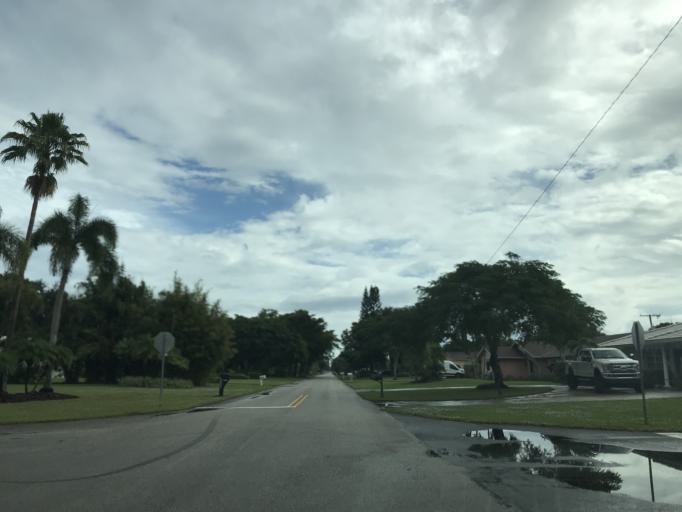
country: US
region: Florida
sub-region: Palm Beach County
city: Kings Point
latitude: 26.4447
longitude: -80.1184
